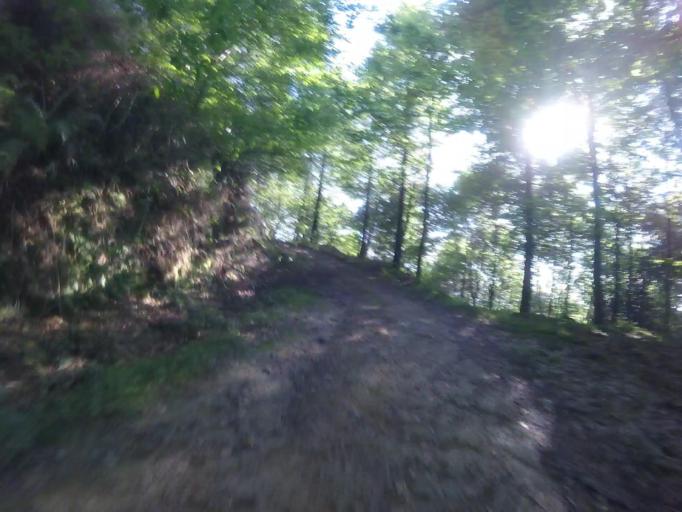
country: ES
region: Navarre
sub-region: Provincia de Navarra
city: Arano
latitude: 43.2423
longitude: -1.9022
